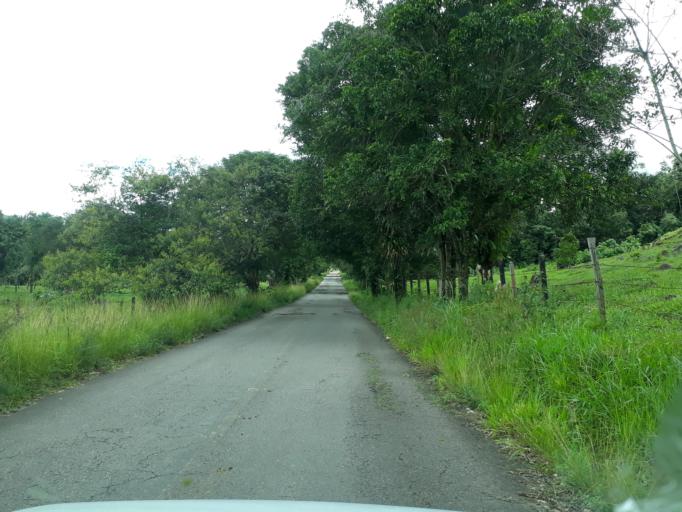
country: CO
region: Cundinamarca
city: Medina
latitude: 4.5414
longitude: -73.3577
